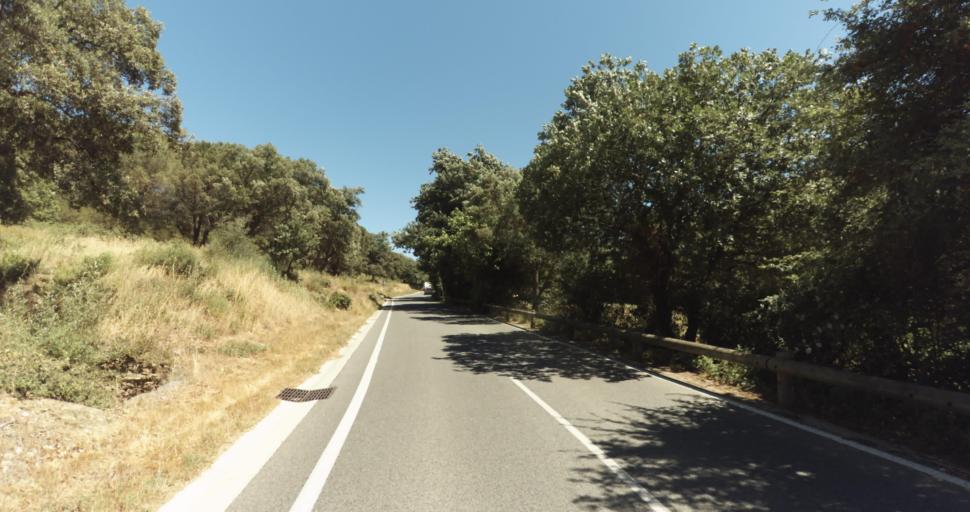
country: FR
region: Provence-Alpes-Cote d'Azur
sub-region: Departement du Var
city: Gassin
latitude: 43.2380
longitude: 6.5699
